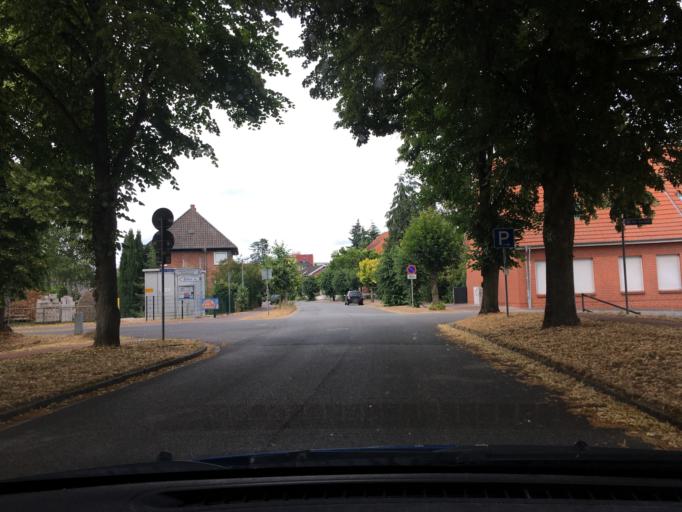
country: DE
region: Mecklenburg-Vorpommern
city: Boizenburg
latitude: 53.3764
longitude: 10.7258
